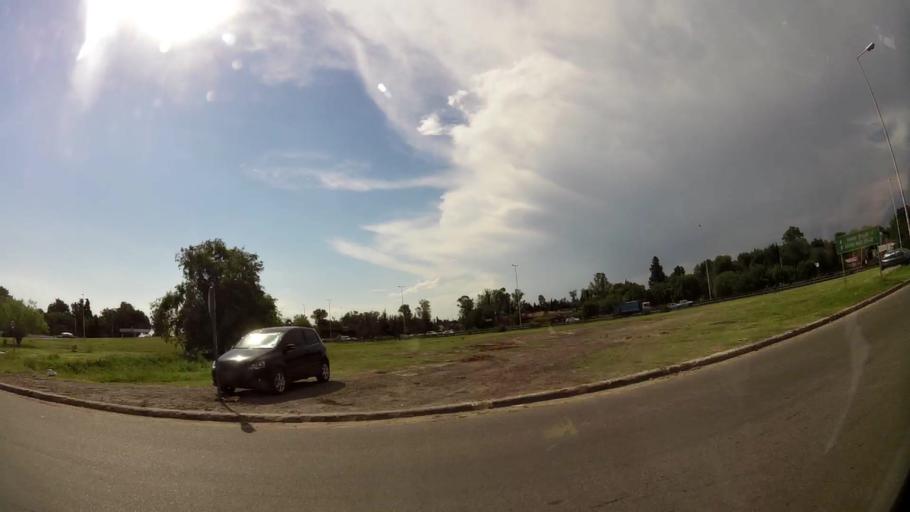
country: AR
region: Buenos Aires
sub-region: Partido de Merlo
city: Merlo
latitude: -34.6294
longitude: -58.7110
